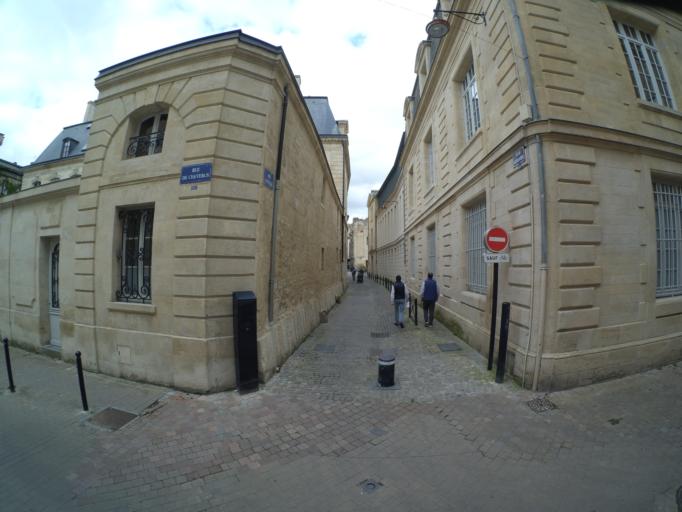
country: FR
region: Aquitaine
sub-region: Departement de la Gironde
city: Bordeaux
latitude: 44.8394
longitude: -0.5759
